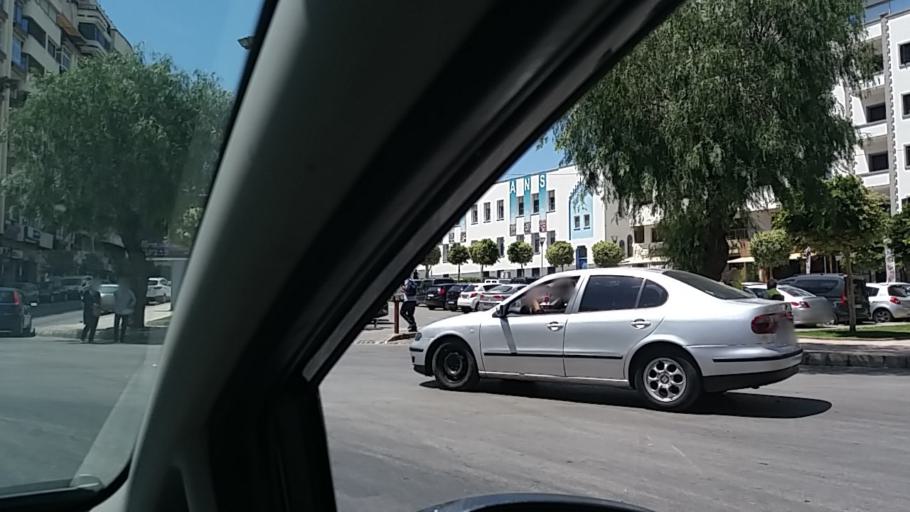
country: MA
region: Tanger-Tetouan
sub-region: Tanger-Assilah
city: Tangier
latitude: 35.7754
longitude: -5.8107
